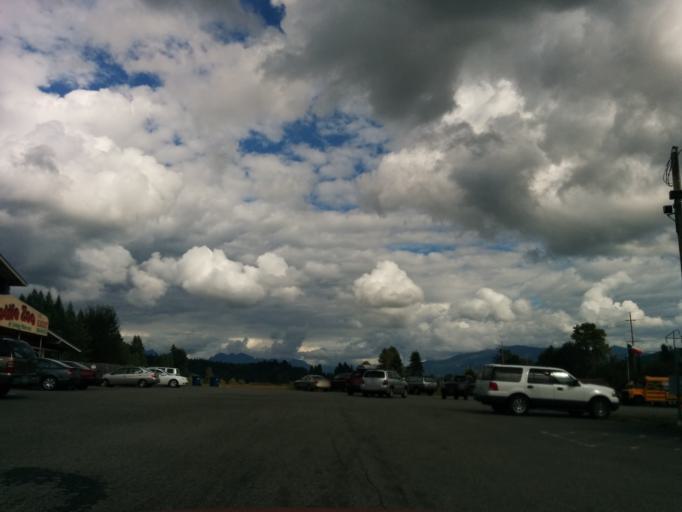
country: US
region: Washington
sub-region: Snohomish County
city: Woods Creek
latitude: 47.8564
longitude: -121.9271
